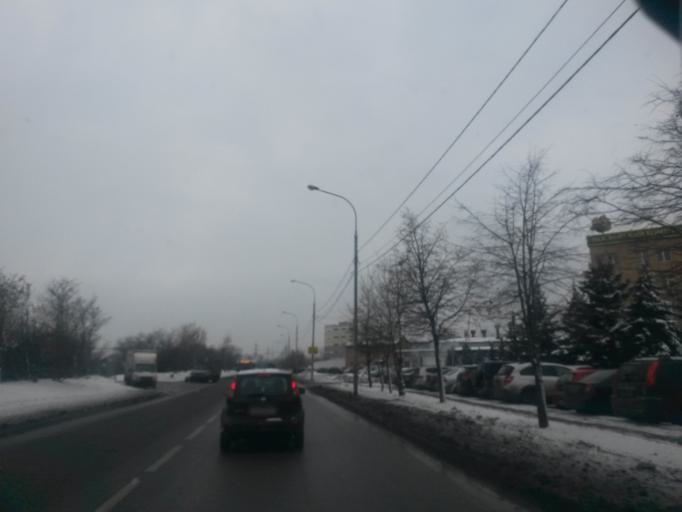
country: RU
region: Moscow
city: Mikhalkovo
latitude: 55.6749
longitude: 37.4366
